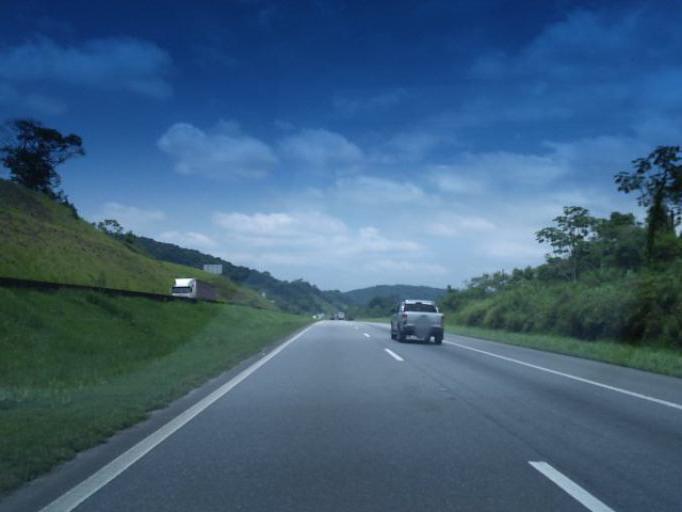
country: BR
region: Sao Paulo
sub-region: Miracatu
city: Miracatu
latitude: -24.1745
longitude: -47.3443
